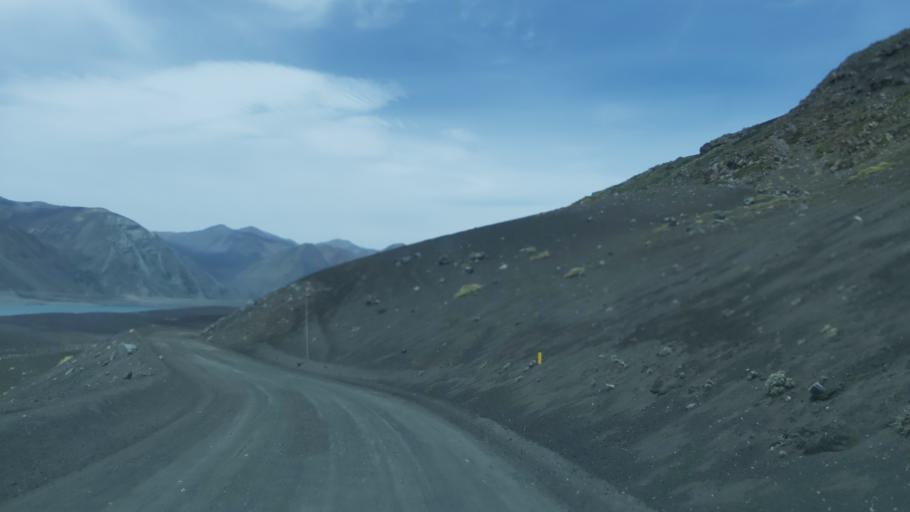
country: AR
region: Neuquen
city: Andacollo
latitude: -37.4068
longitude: -71.2995
